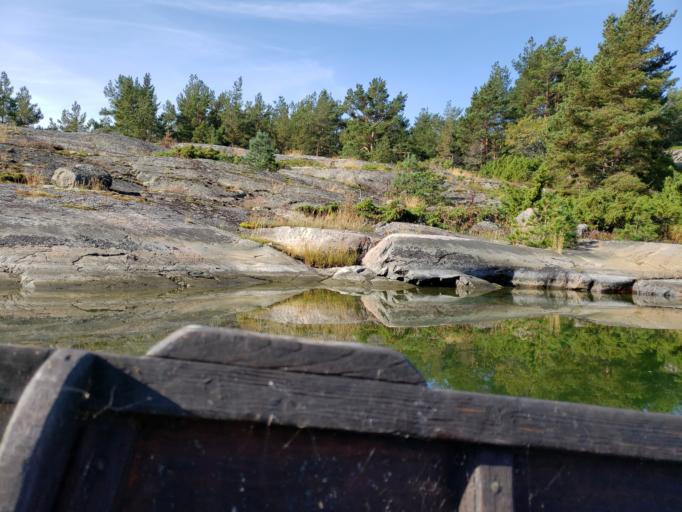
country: FI
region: Varsinais-Suomi
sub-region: Aboland-Turunmaa
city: Dragsfjaerd
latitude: 59.8584
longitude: 22.2091
